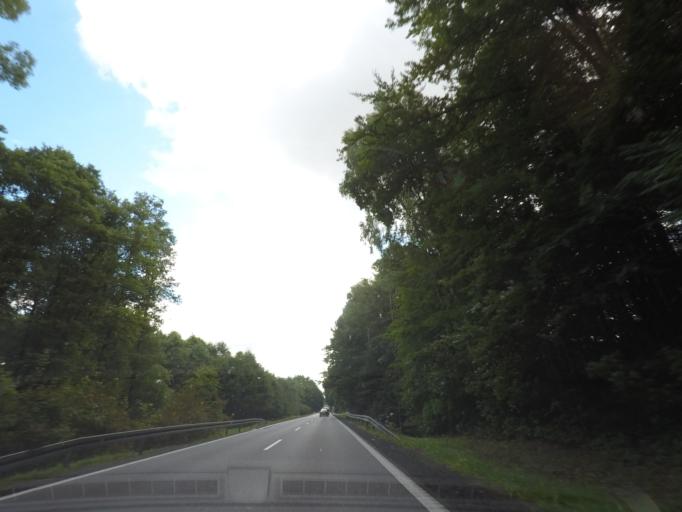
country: PL
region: Pomeranian Voivodeship
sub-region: Powiat wejherowski
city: Leczyce
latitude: 54.5739
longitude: 17.9226
